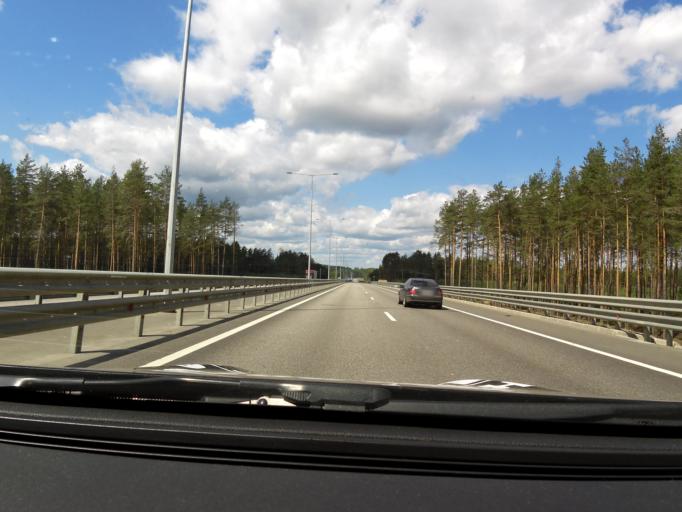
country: RU
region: Tverskaya
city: Vydropuzhsk
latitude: 57.2781
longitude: 34.8293
